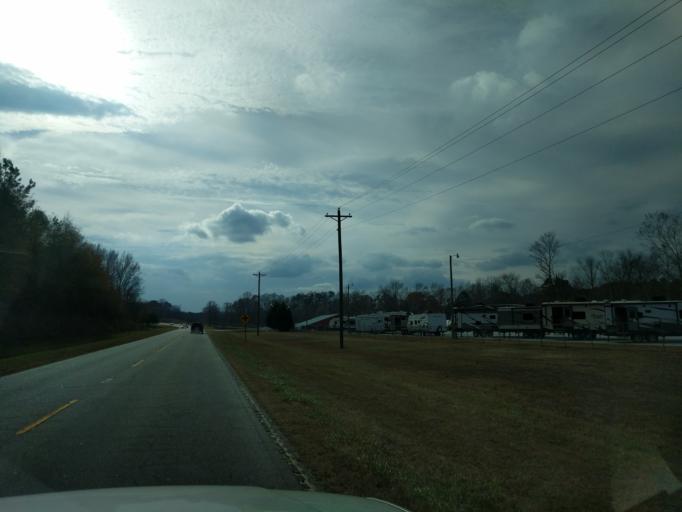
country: US
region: South Carolina
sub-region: Oconee County
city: Westminster
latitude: 34.6560
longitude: -83.0434
